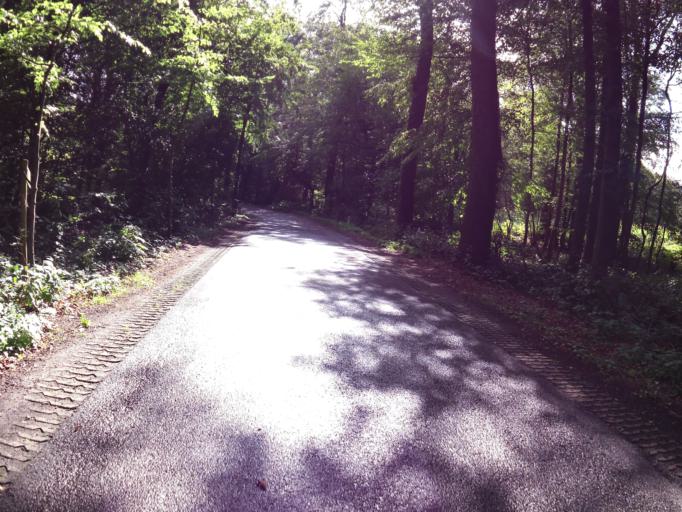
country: NL
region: Gelderland
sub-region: Gemeente Aalten
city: Bredevoort
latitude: 51.9631
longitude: 6.6297
